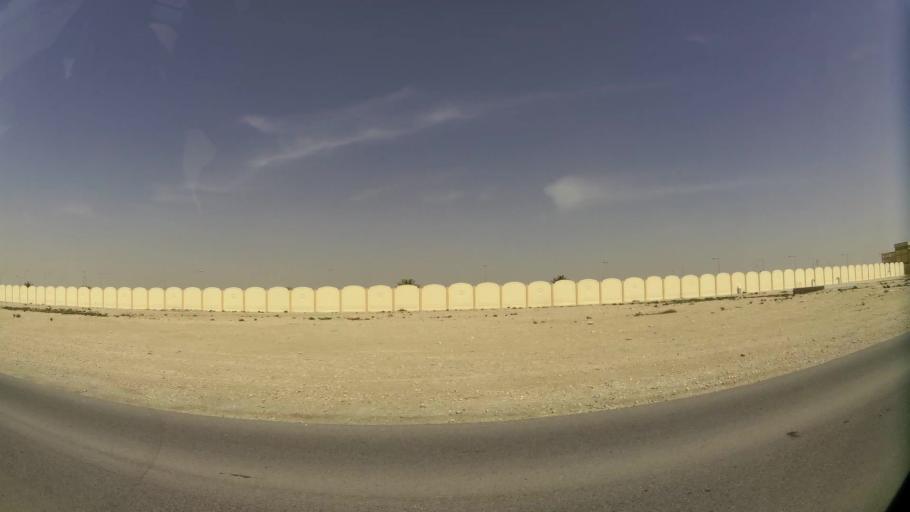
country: QA
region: Baladiyat ar Rayyan
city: Ar Rayyan
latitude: 25.2542
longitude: 51.3848
